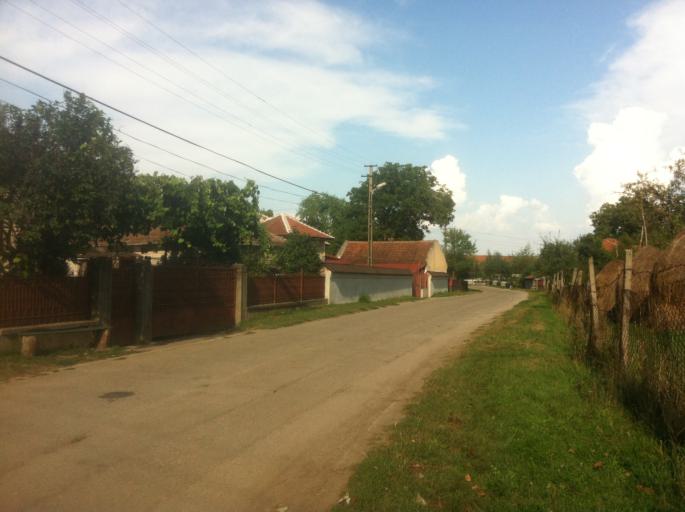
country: RO
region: Hunedoara
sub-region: Comuna Sarmizegetusa
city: Sarmizegetusa
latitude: 45.5396
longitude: 22.8182
